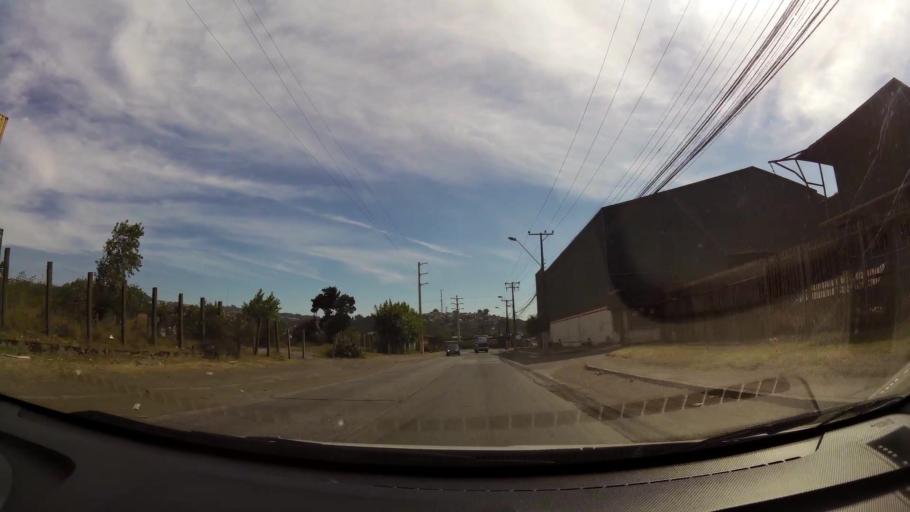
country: CL
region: Biobio
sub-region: Provincia de Concepcion
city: Talcahuano
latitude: -36.7276
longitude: -73.1170
